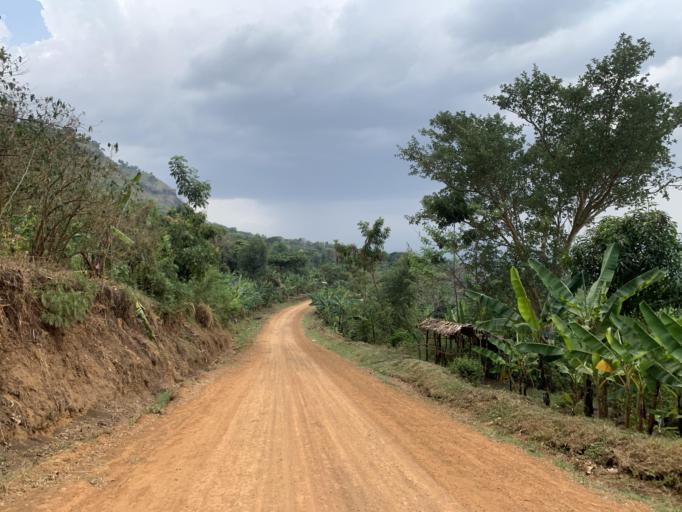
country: UG
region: Eastern Region
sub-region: Sironko District
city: Sironko
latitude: 1.2599
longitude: 34.2916
